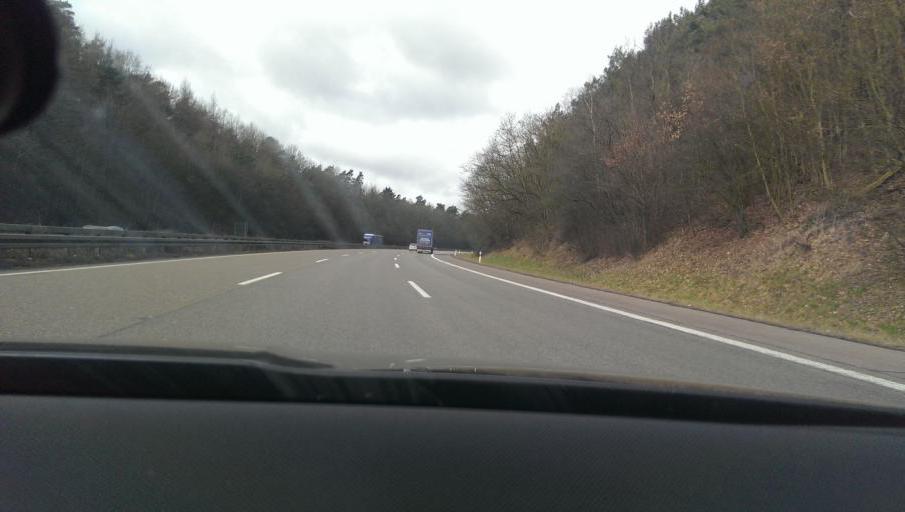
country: DE
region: Hesse
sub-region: Regierungsbezirk Kassel
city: Niederaula
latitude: 50.7843
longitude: 9.5552
